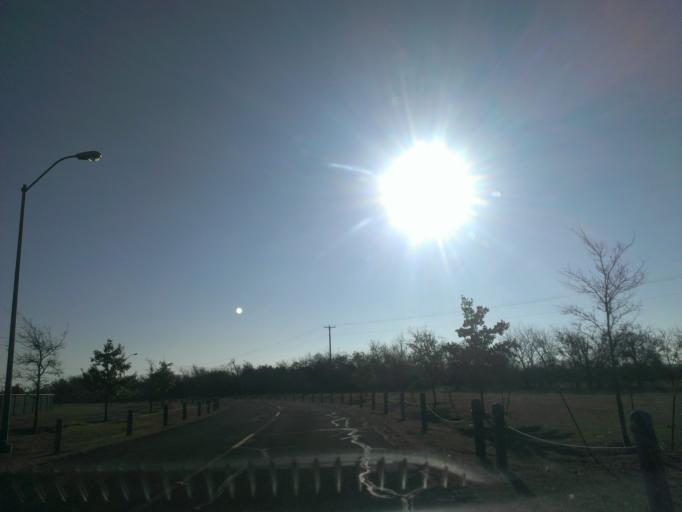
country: US
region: Texas
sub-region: Williamson County
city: Round Rock
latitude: 30.5407
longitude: -97.6211
